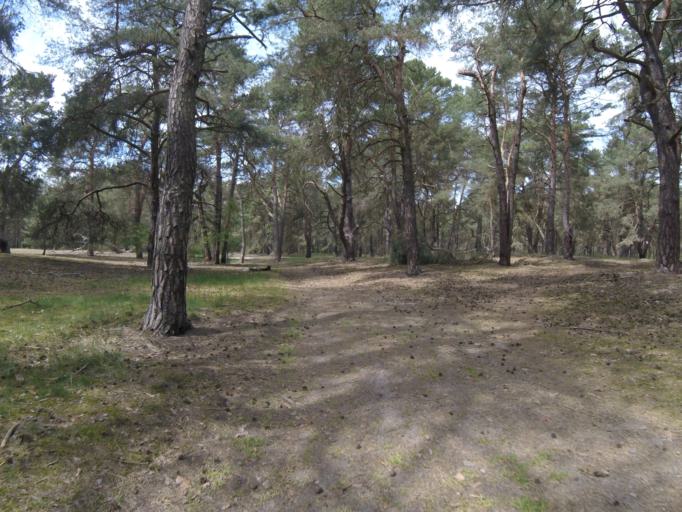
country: DE
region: Brandenburg
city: Bestensee
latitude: 52.2220
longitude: 13.6292
